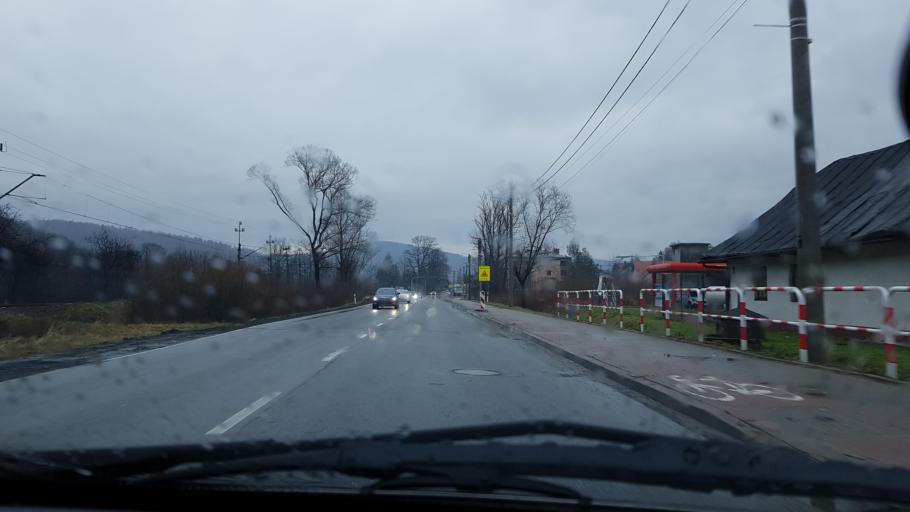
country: PL
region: Lesser Poland Voivodeship
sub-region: Powiat suski
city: Sucha Beskidzka
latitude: 49.7374
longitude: 19.5693
